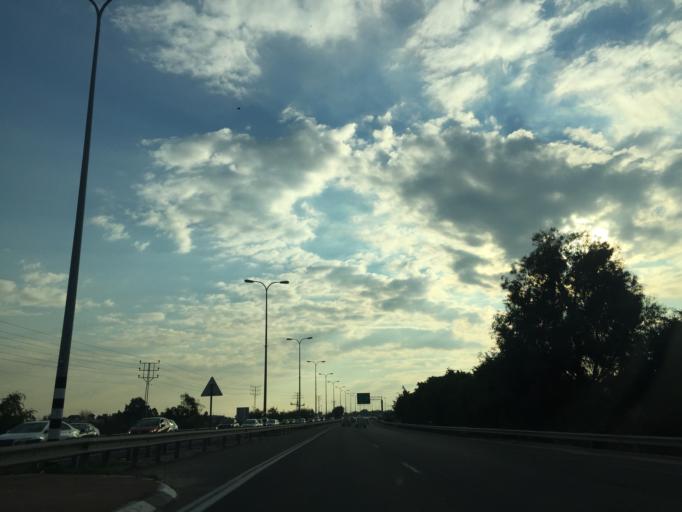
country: IL
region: Central District
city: Lod
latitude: 31.9318
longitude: 34.8907
